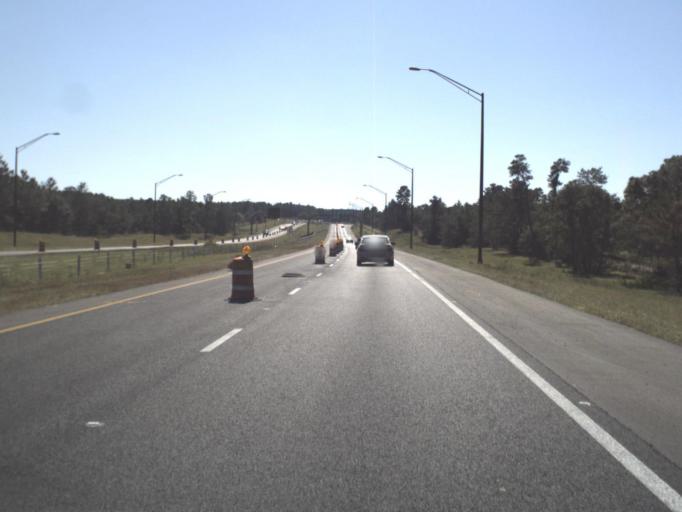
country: US
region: Florida
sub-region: Citrus County
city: Sugarmill Woods
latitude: 28.6761
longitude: -82.4967
